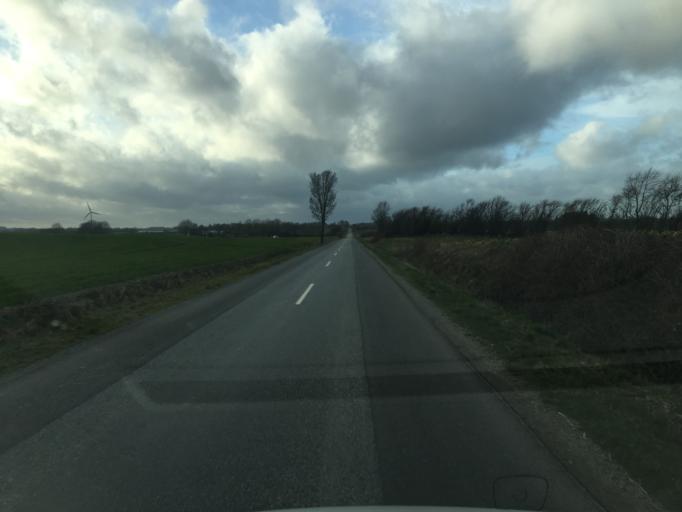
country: DK
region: South Denmark
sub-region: Sonderborg Kommune
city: Grasten
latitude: 54.9651
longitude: 9.5356
